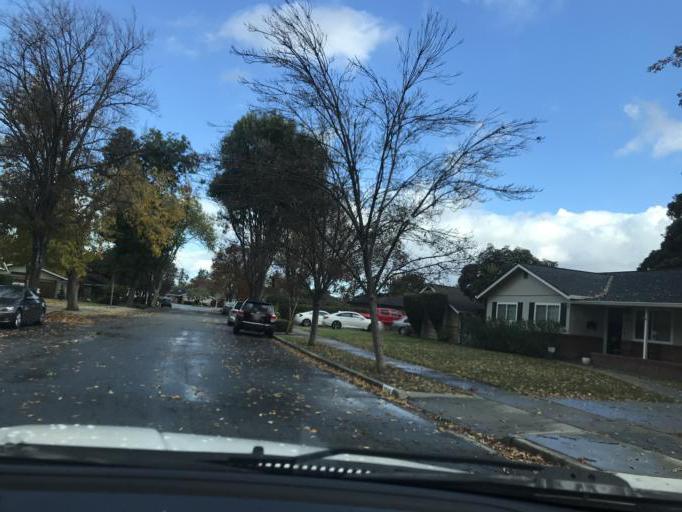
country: US
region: California
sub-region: Santa Clara County
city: Buena Vista
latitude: 37.2967
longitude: -121.9170
